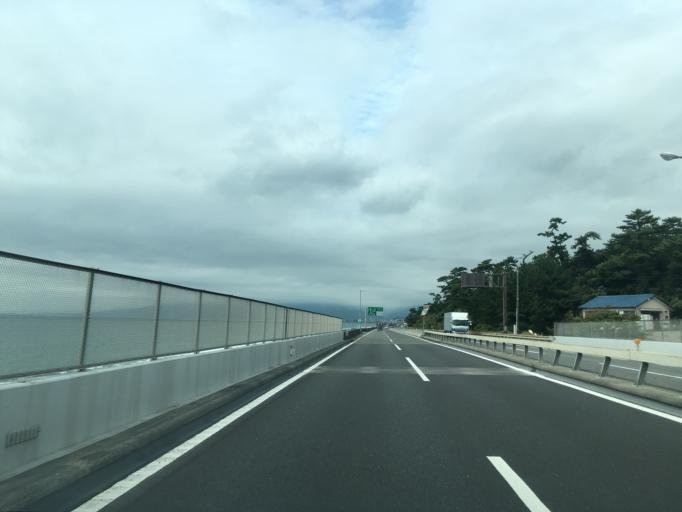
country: JP
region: Kanagawa
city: Ninomiya
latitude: 35.2926
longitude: 139.2483
